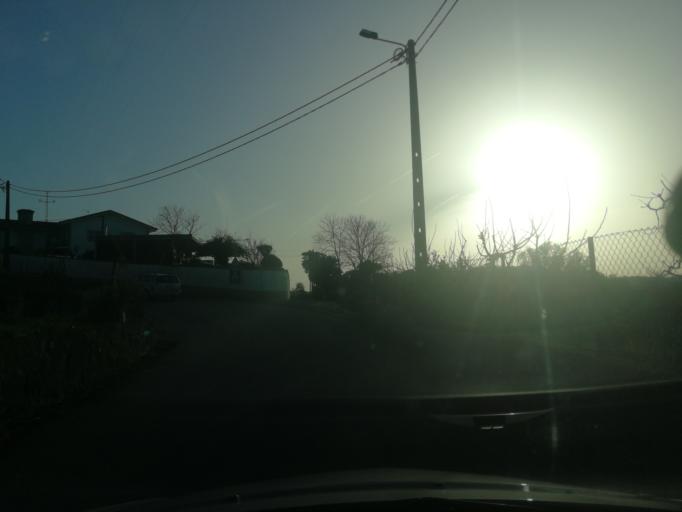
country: PT
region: Braga
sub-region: Barcelos
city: Galegos
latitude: 41.5149
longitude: -8.5616
